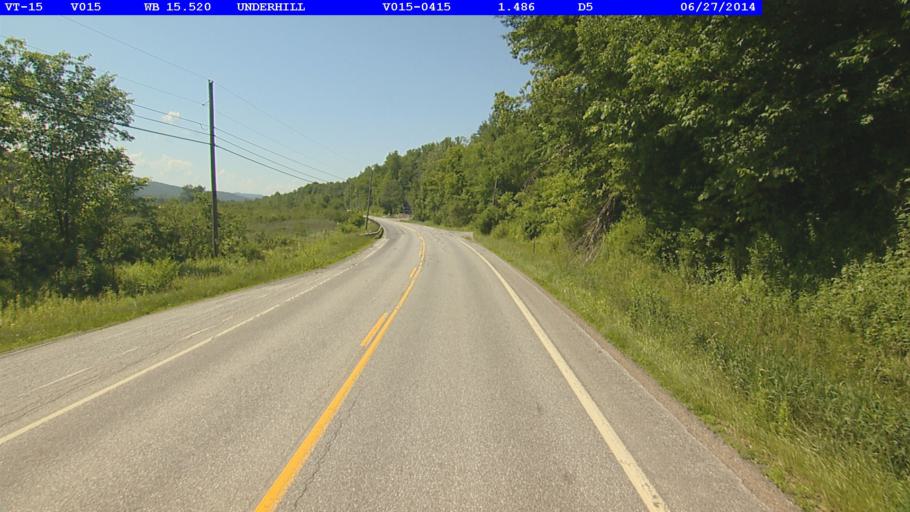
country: US
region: Vermont
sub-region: Chittenden County
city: Jericho
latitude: 44.5457
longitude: -72.9480
